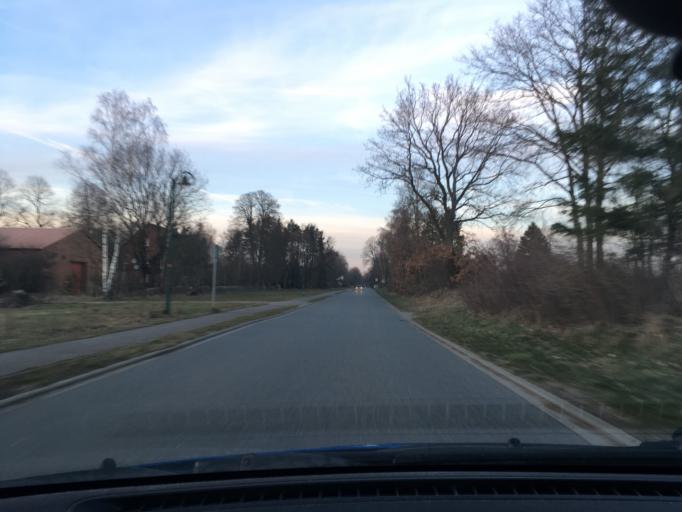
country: DE
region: Schleswig-Holstein
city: Langenlehsten
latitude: 53.4984
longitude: 10.7400
